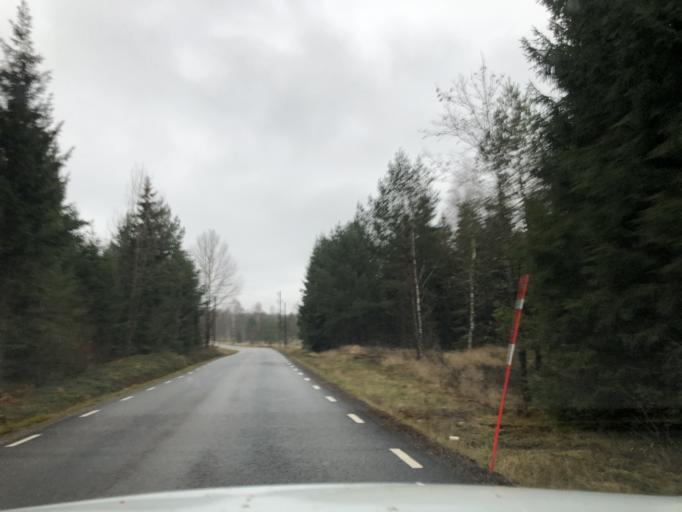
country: SE
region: Vaestra Goetaland
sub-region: Ulricehamns Kommun
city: Ulricehamn
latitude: 57.8268
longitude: 13.4160
